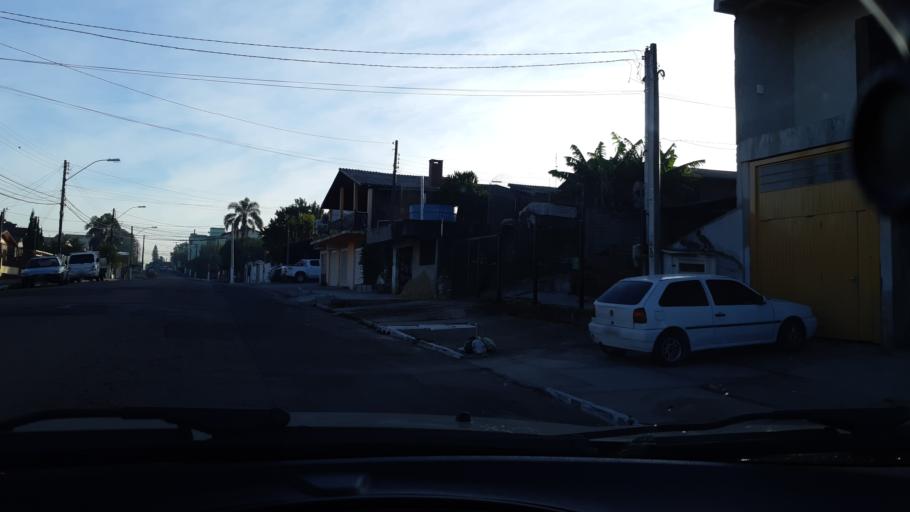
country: BR
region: Rio Grande do Sul
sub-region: Sapucaia Do Sul
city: Sapucaia
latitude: -29.8480
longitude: -51.1526
